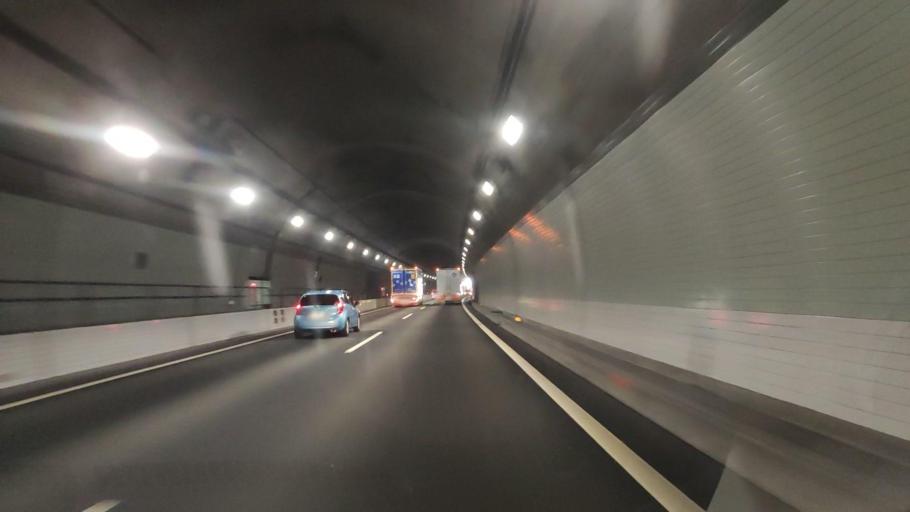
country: JP
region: Tokyo
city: Itsukaichi
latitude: 35.7020
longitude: 139.2726
